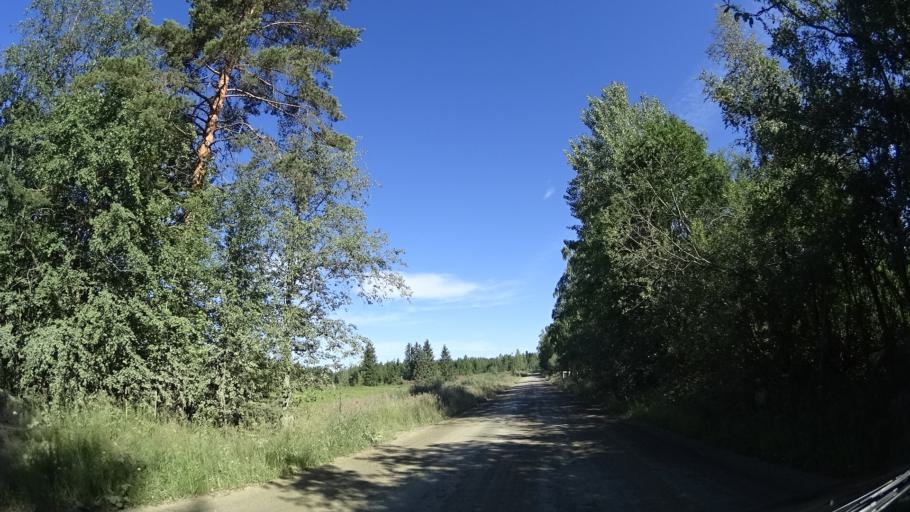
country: FI
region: Central Finland
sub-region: Jyvaeskylae
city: Petaejaevesi
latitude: 62.3566
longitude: 25.3224
